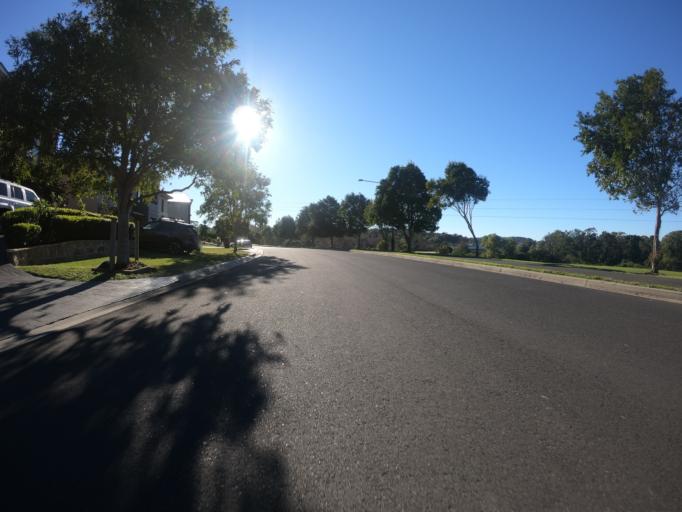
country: AU
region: New South Wales
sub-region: Wollongong
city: Cordeaux Heights
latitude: -34.4383
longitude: 150.8477
